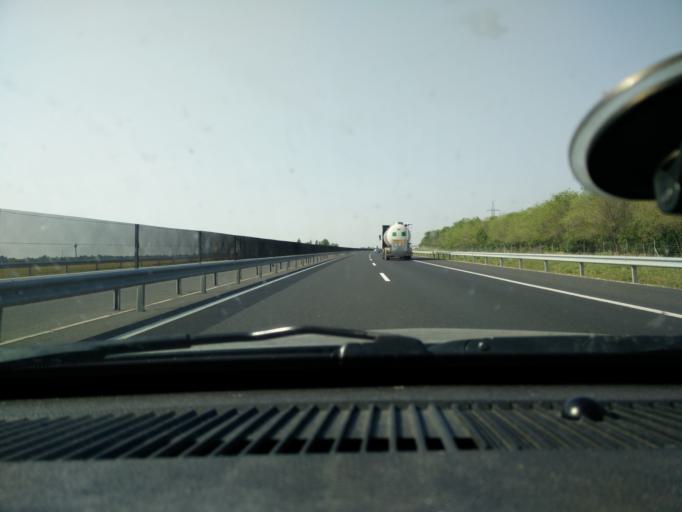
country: HU
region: Fejer
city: Ivancsa
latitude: 47.1960
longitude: 18.8160
